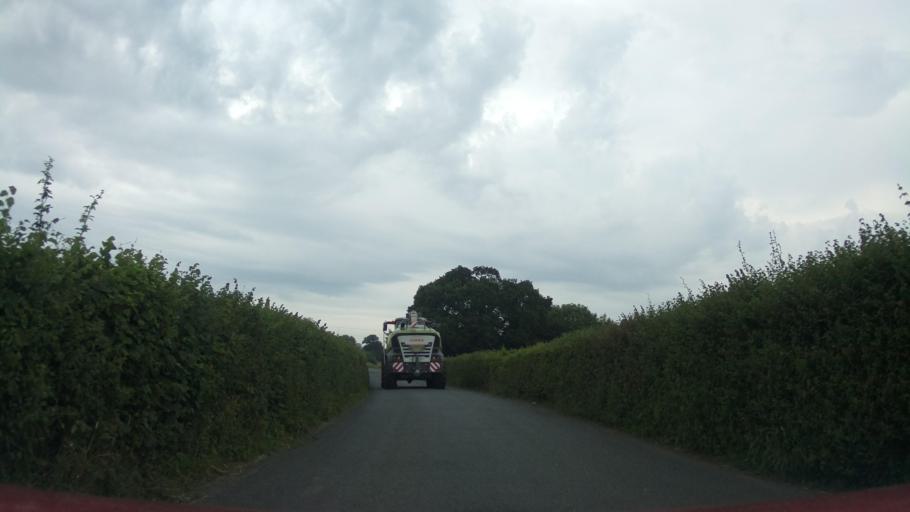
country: GB
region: England
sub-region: Somerset
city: Yeovil
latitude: 50.9136
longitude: -2.5831
